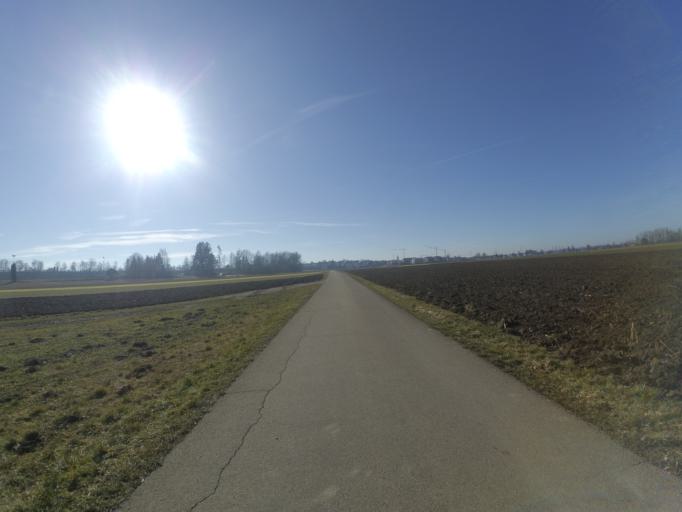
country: DE
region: Baden-Wuerttemberg
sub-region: Tuebingen Region
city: Erbach
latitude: 48.3126
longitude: 9.9074
